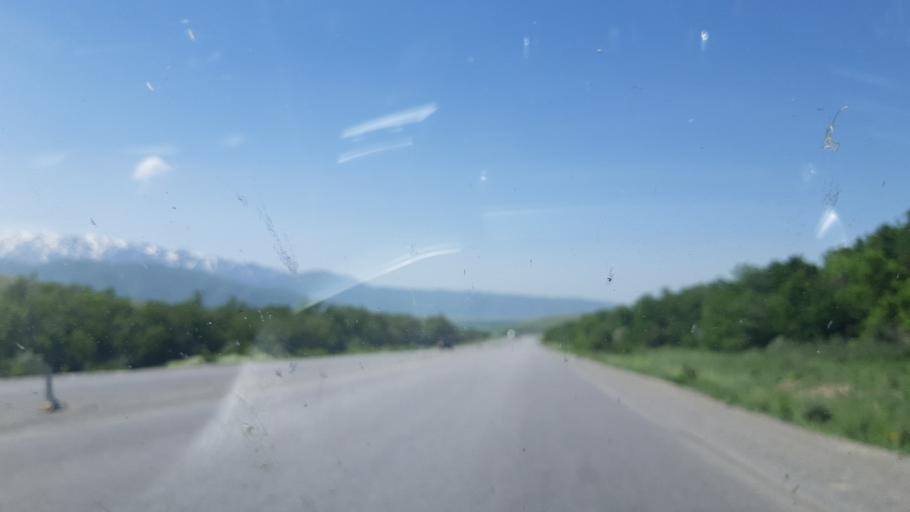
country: KZ
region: Ongtustik Qazaqstan
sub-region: Tulkibas Audany
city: Zhabagly
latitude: 42.5322
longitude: 70.6031
